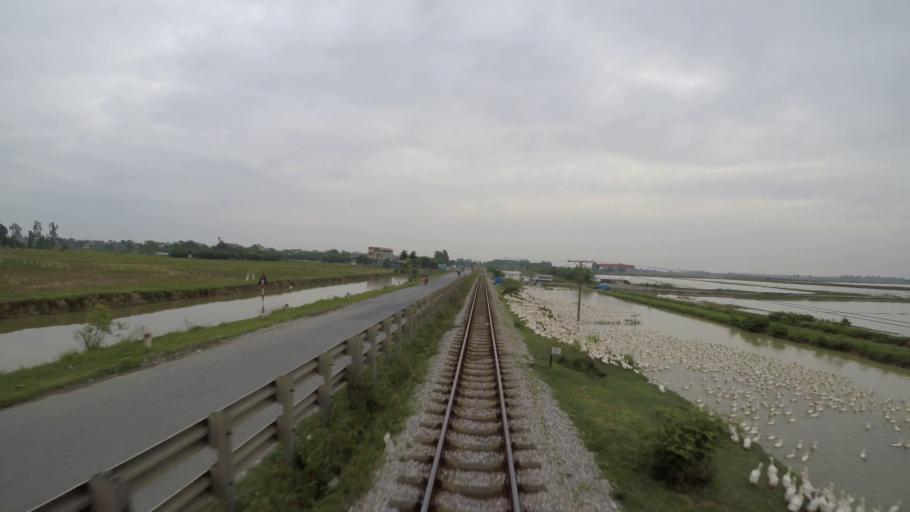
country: VN
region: Hung Yen
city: Ban Yen Nhan
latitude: 20.9846
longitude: 106.0714
